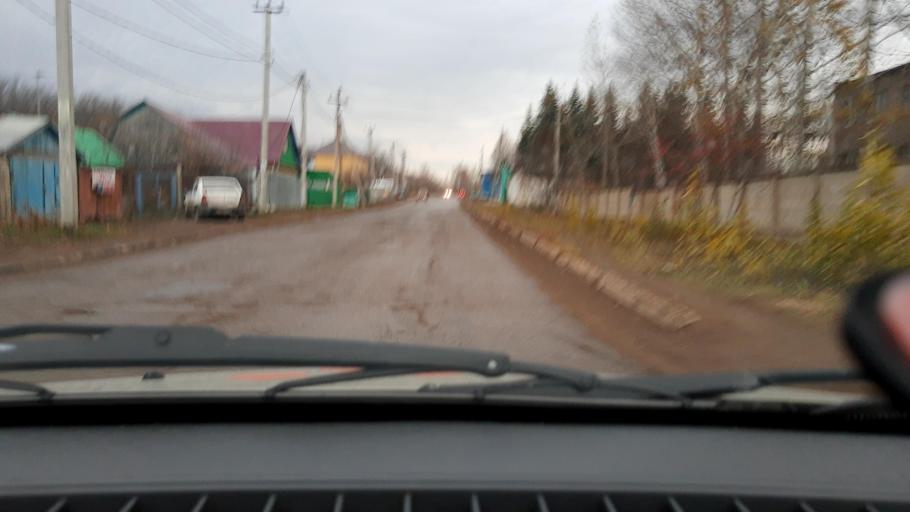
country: RU
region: Bashkortostan
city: Avdon
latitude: 54.6830
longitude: 55.7963
